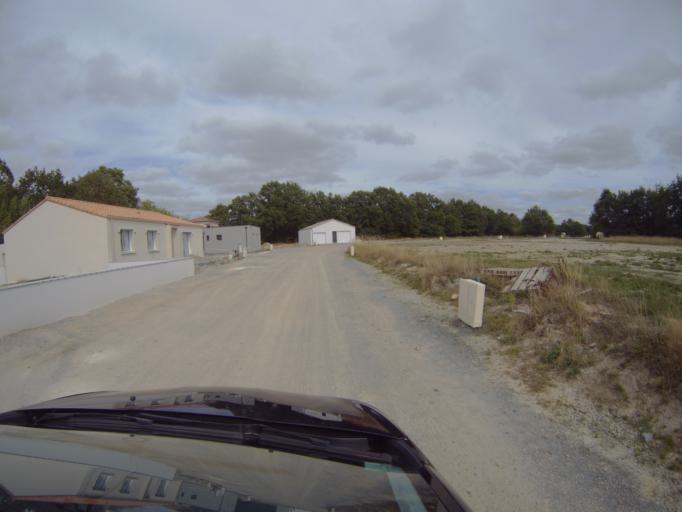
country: FR
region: Pays de la Loire
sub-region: Departement de la Vendee
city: Saint-Hilaire-de-Loulay
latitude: 46.9971
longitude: -1.3371
